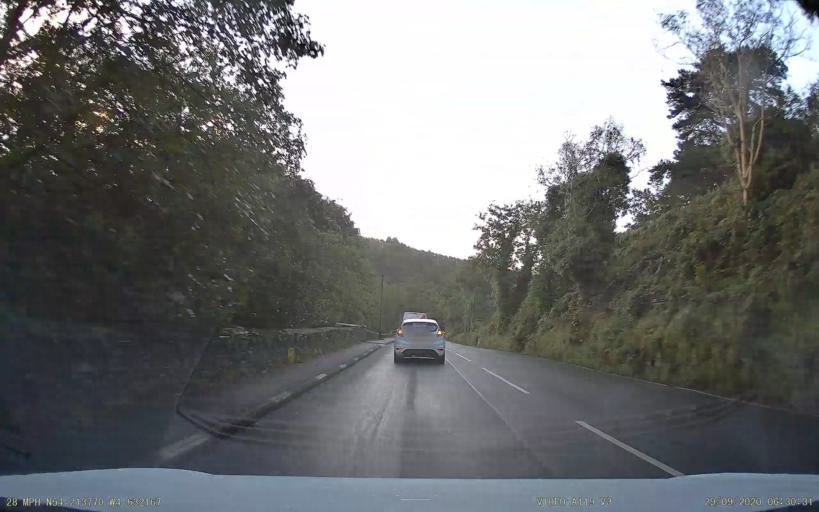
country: IM
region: Castletown
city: Castletown
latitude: 54.2138
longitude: -4.6322
